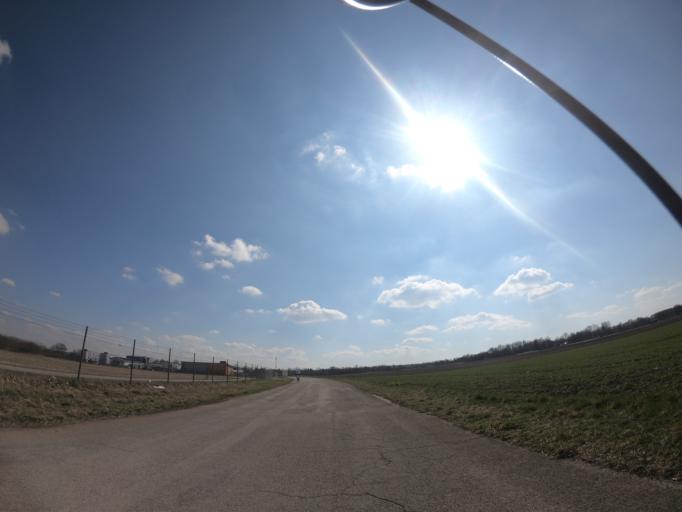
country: DE
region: Bavaria
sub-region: Upper Bavaria
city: Maisach
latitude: 48.2044
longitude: 11.2417
